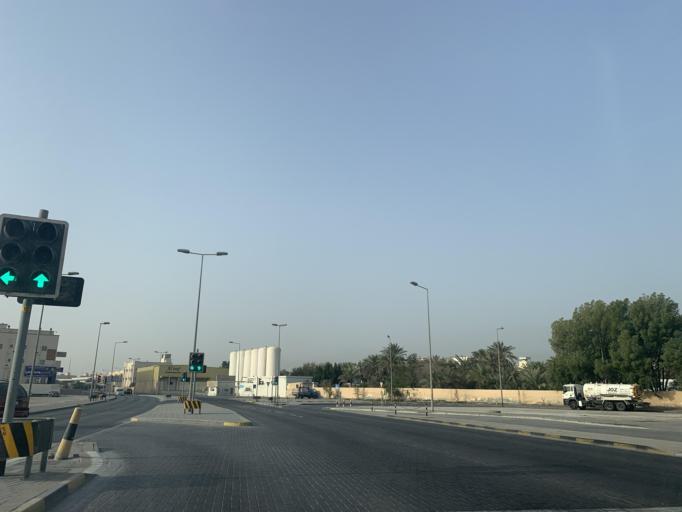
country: BH
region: Northern
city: Madinat `Isa
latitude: 26.1933
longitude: 50.5565
